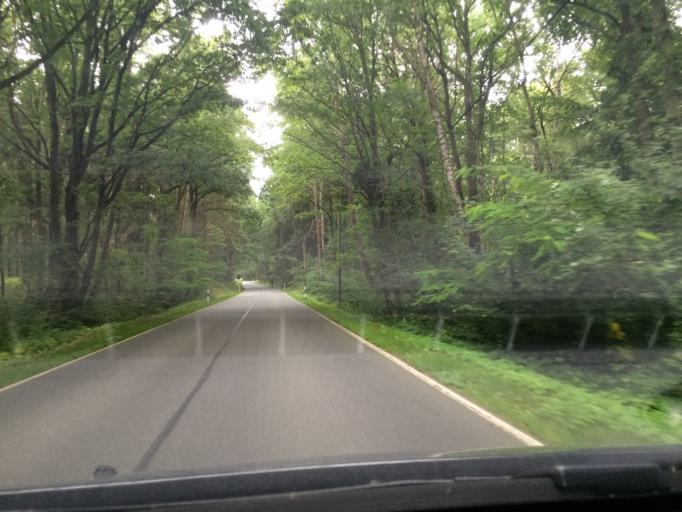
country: DE
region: Mecklenburg-Vorpommern
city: Prohn
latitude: 54.4262
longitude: 13.0242
